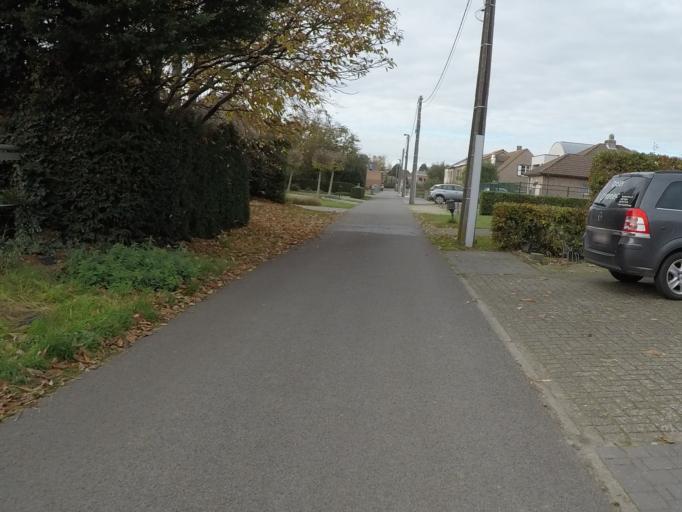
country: BE
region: Flanders
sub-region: Provincie Antwerpen
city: Nijlen
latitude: 51.1549
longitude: 4.6675
